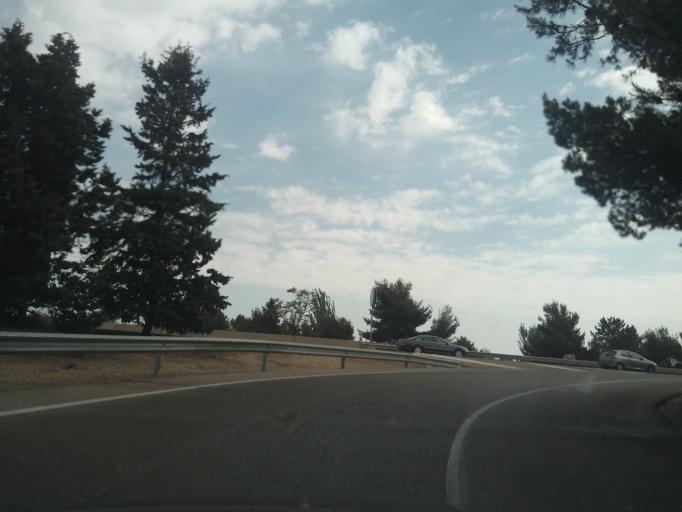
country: ES
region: Madrid
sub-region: Provincia de Madrid
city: Pinar de Chamartin
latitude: 40.4834
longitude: -3.6747
